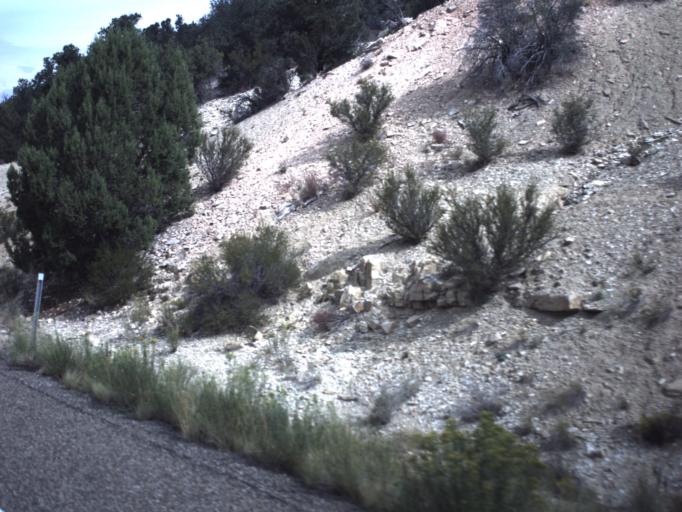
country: US
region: Utah
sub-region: Kane County
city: Kanab
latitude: 37.1997
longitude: -112.6690
